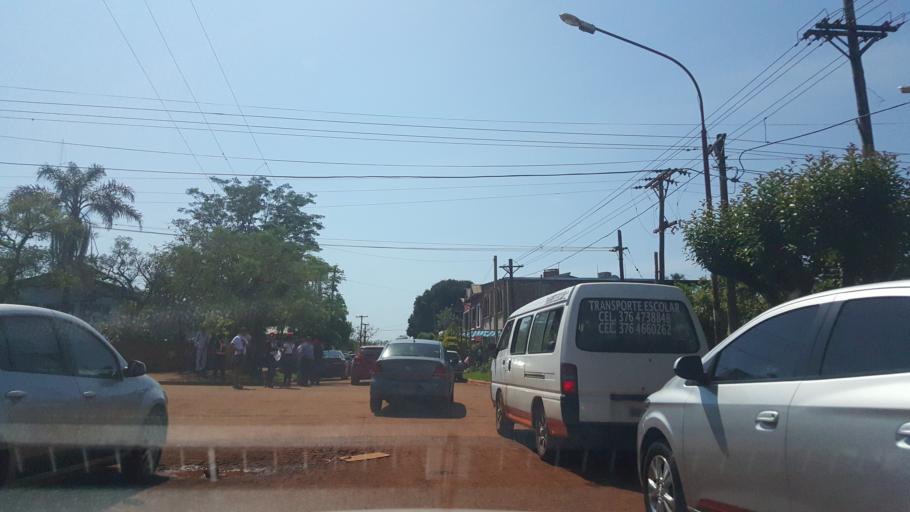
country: AR
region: Corrientes
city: San Carlos
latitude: -27.7452
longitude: -55.8991
